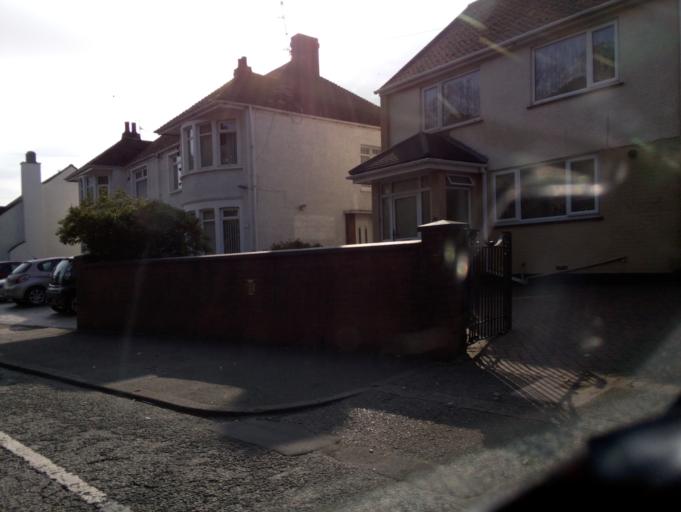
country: GB
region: Wales
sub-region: Cardiff
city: Cardiff
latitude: 51.5109
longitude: -3.1313
